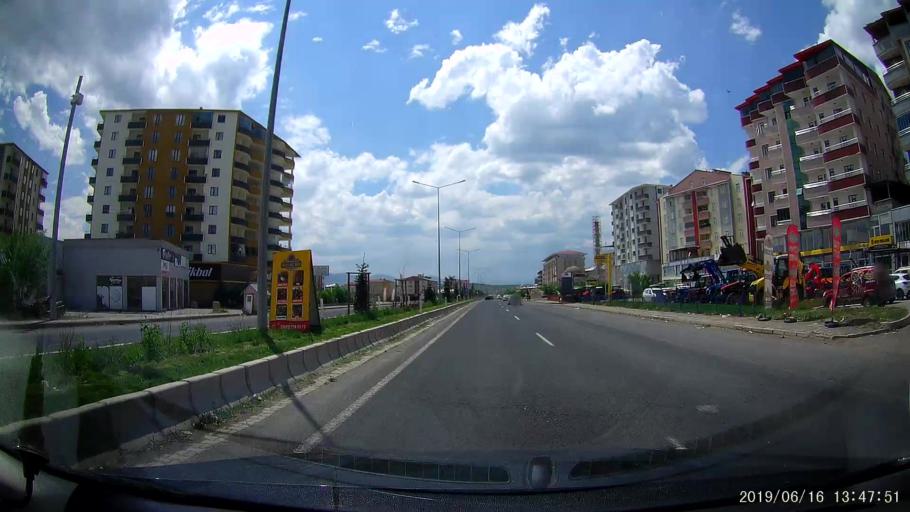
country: TR
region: Agri
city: Agri
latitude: 39.7143
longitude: 43.0181
